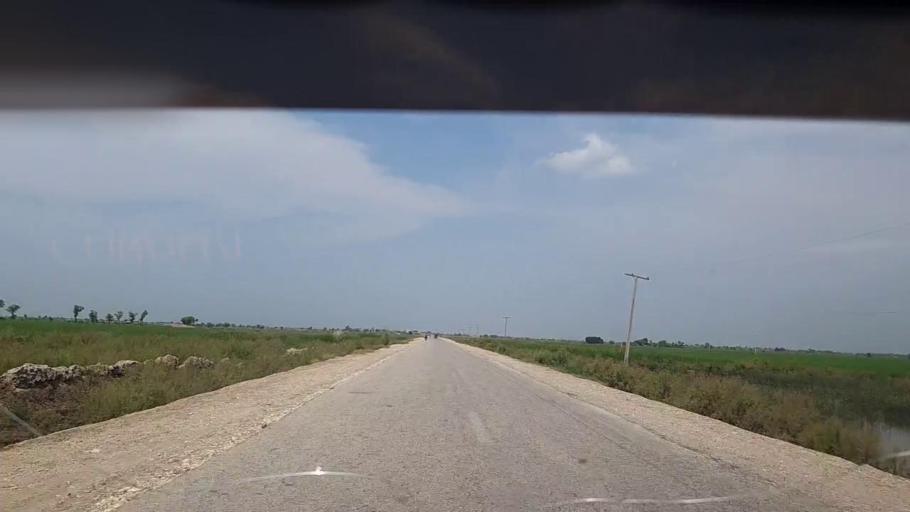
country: PK
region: Sindh
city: Thul
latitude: 28.1898
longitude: 68.7959
